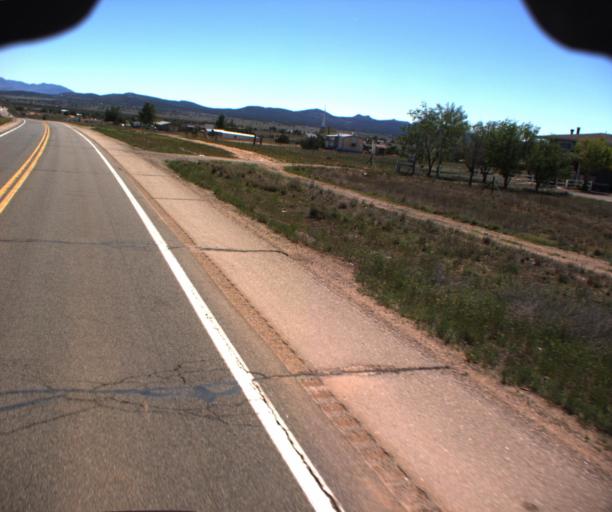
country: US
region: Arizona
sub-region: Yavapai County
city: Paulden
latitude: 34.9080
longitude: -112.4619
